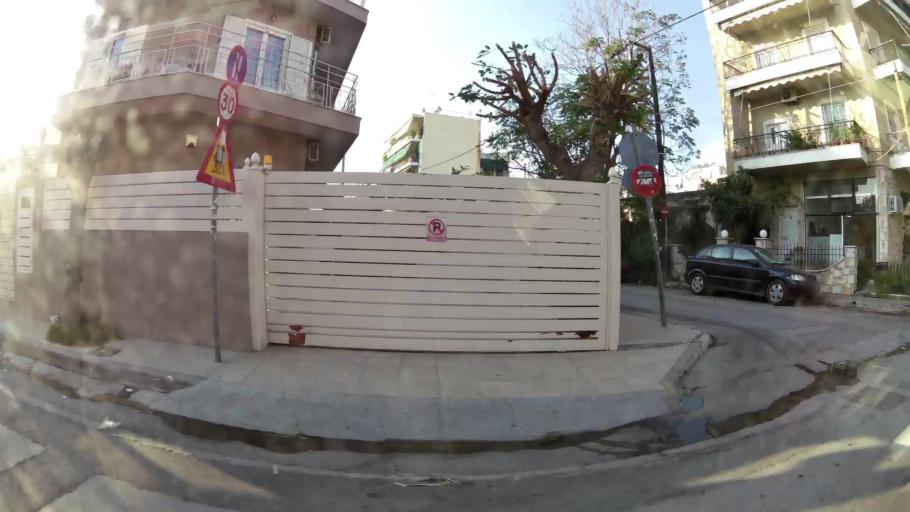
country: GR
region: Attica
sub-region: Nomarchia Anatolikis Attikis
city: Acharnes
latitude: 38.0874
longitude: 23.7415
